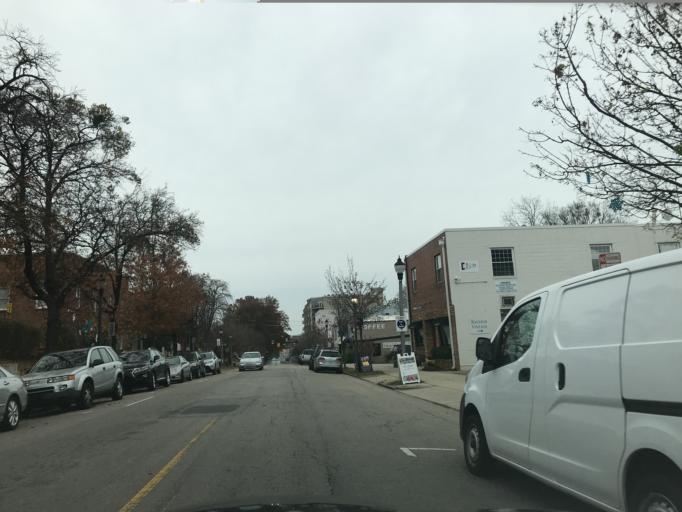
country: US
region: North Carolina
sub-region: Wake County
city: Raleigh
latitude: 35.7813
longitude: -78.6475
